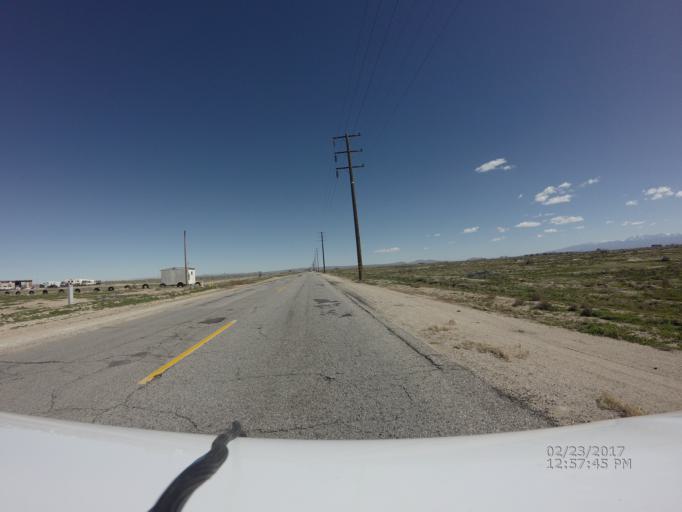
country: US
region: California
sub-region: Los Angeles County
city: Lancaster
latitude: 34.7630
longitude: -118.0494
